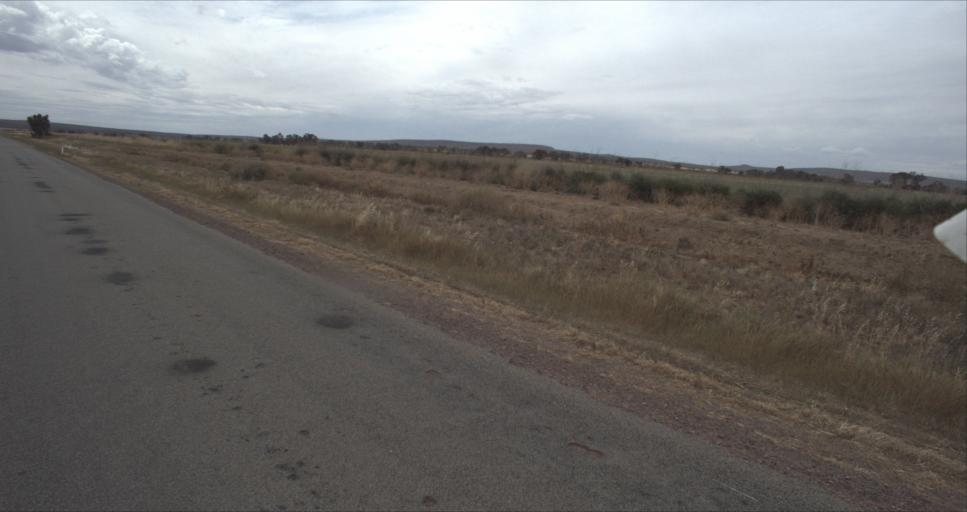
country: AU
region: New South Wales
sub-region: Leeton
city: Leeton
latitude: -34.4970
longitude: 146.4004
